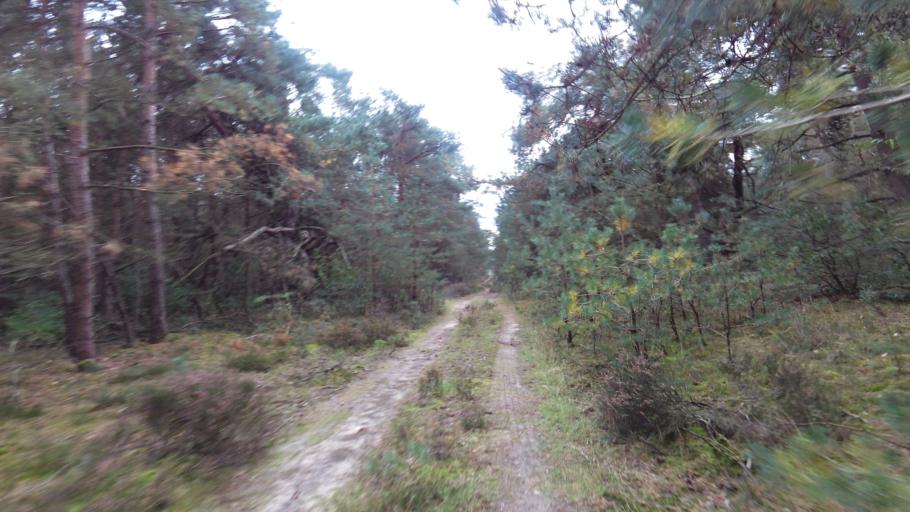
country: NL
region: Gelderland
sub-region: Gemeente Barneveld
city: Stroe
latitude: 52.1914
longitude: 5.7217
